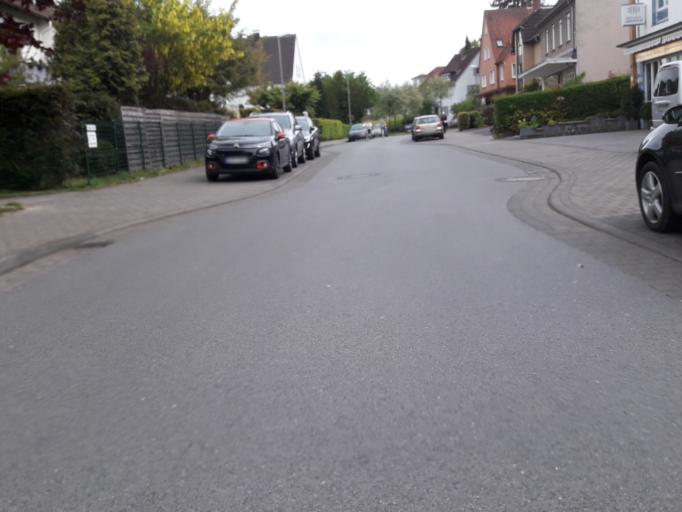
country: DE
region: North Rhine-Westphalia
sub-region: Regierungsbezirk Detmold
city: Detmold
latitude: 51.9401
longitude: 8.8629
